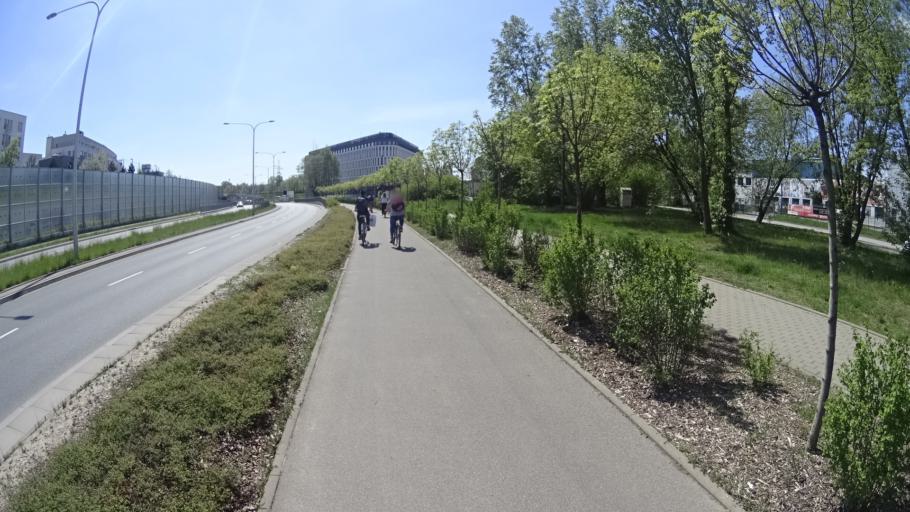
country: PL
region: Masovian Voivodeship
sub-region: Warszawa
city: Ursus
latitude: 52.2076
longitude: 20.8919
